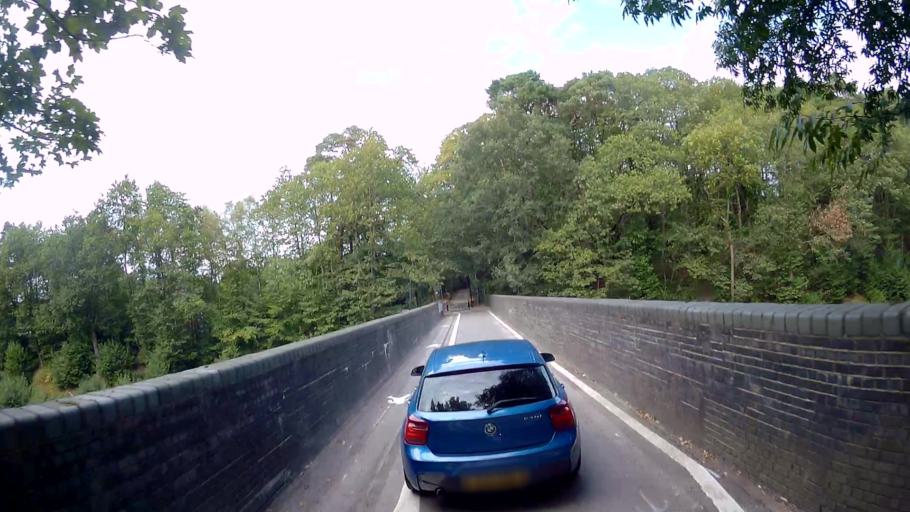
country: GB
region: England
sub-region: Surrey
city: Frimley
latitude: 51.3005
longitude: -0.7100
